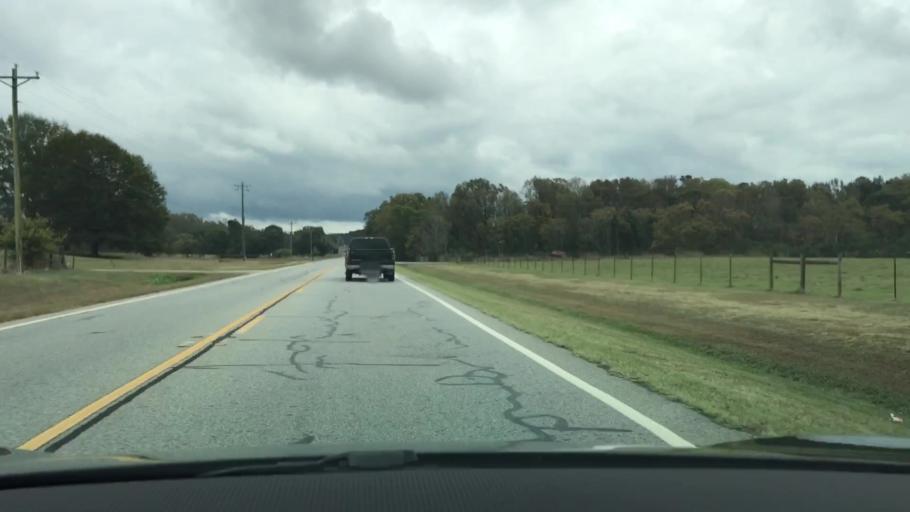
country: US
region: Georgia
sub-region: Oconee County
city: Watkinsville
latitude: 33.8248
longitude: -83.3711
